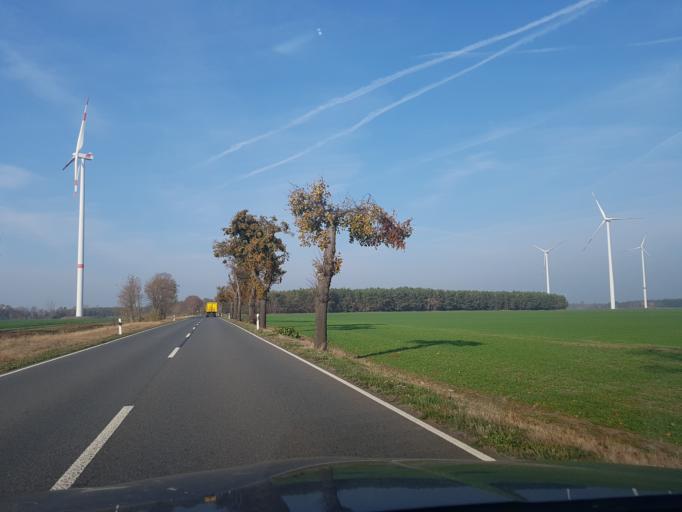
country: DE
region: Brandenburg
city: Bad Liebenwerda
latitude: 51.5247
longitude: 13.3342
